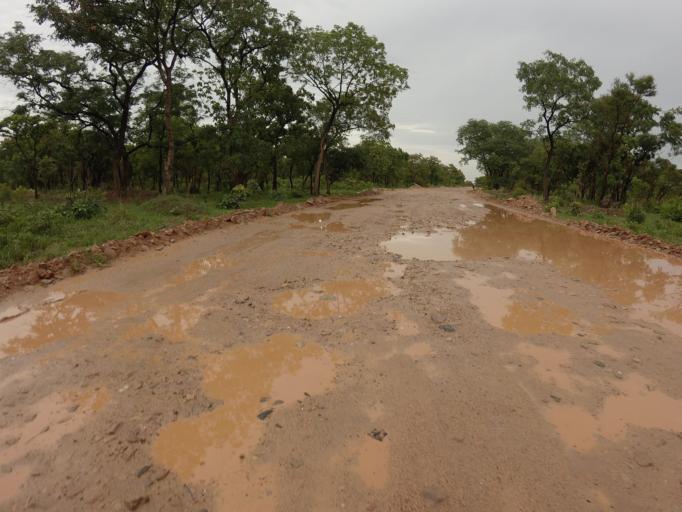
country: GH
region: Upper East
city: Bolgatanga
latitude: 10.8783
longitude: -0.6358
